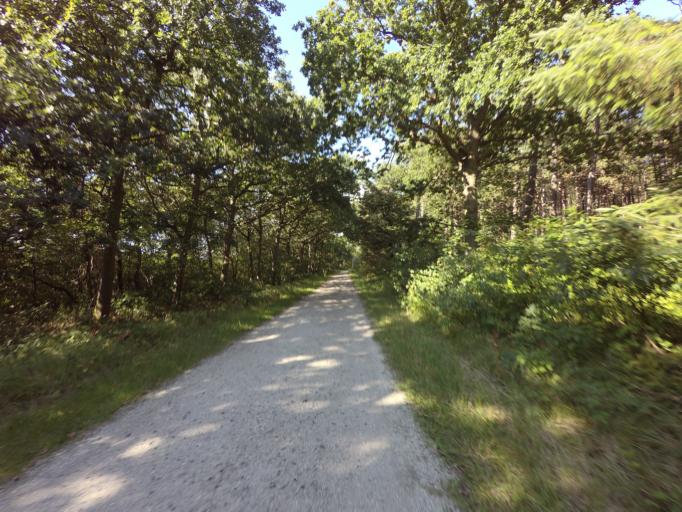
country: NL
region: Friesland
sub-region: Gemeente Terschelling
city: West-Terschelling
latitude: 53.3784
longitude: 5.2382
